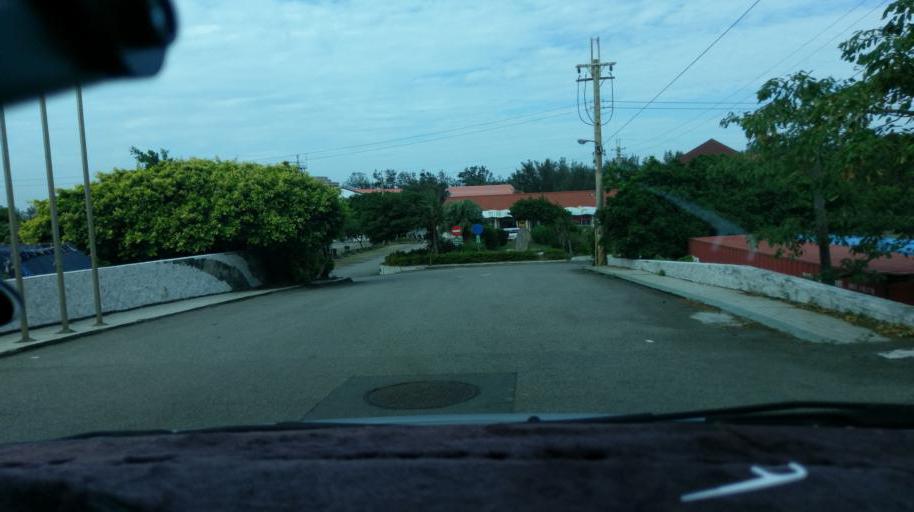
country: TW
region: Taiwan
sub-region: Hsinchu
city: Hsinchu
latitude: 24.7221
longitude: 120.8684
